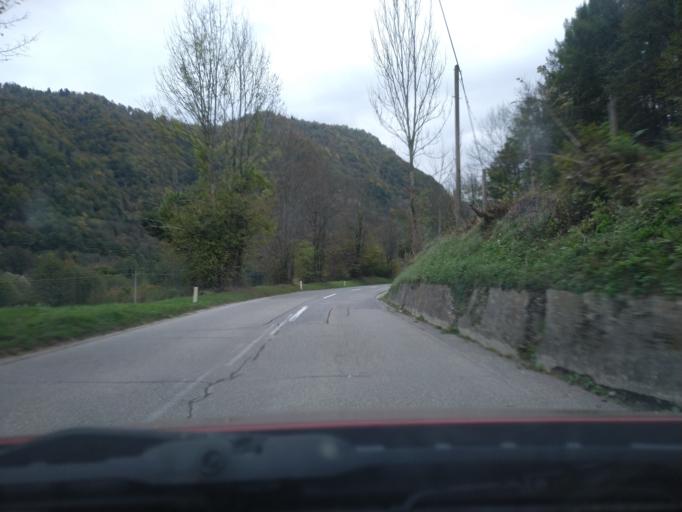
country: SI
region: Tolmin
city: Tolmin
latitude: 46.1601
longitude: 13.7135
